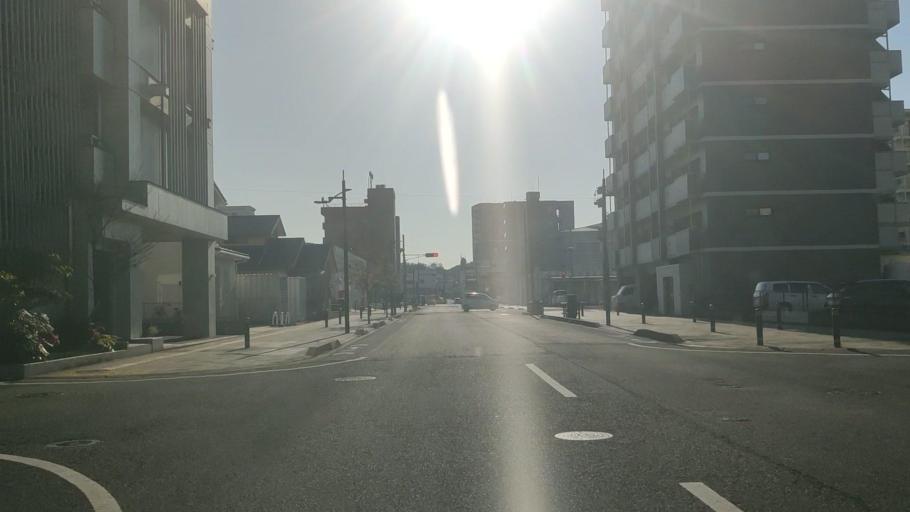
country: JP
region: Oita
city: Oita
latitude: 33.2320
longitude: 131.6027
